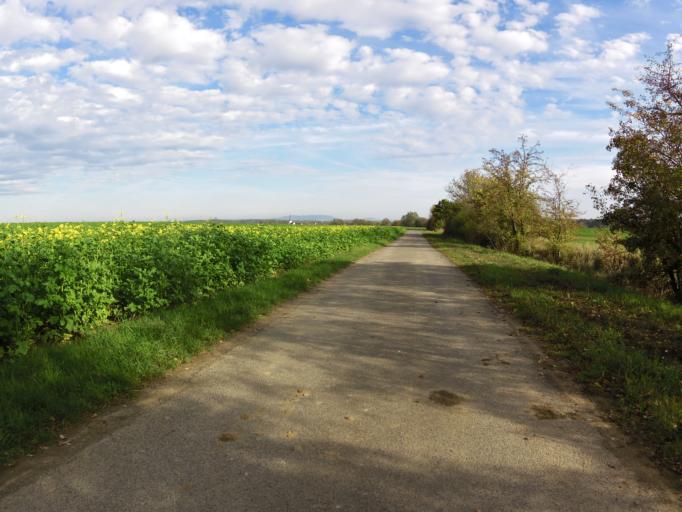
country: DE
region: Bavaria
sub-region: Regierungsbezirk Unterfranken
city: Biebelried
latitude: 49.7284
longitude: 10.0723
